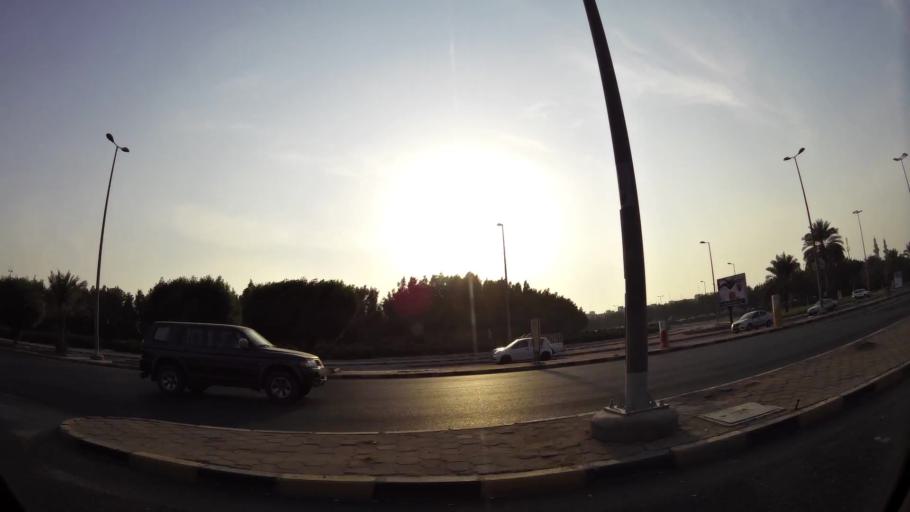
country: KW
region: Mubarak al Kabir
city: Sabah as Salim
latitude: 29.2490
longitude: 48.0680
